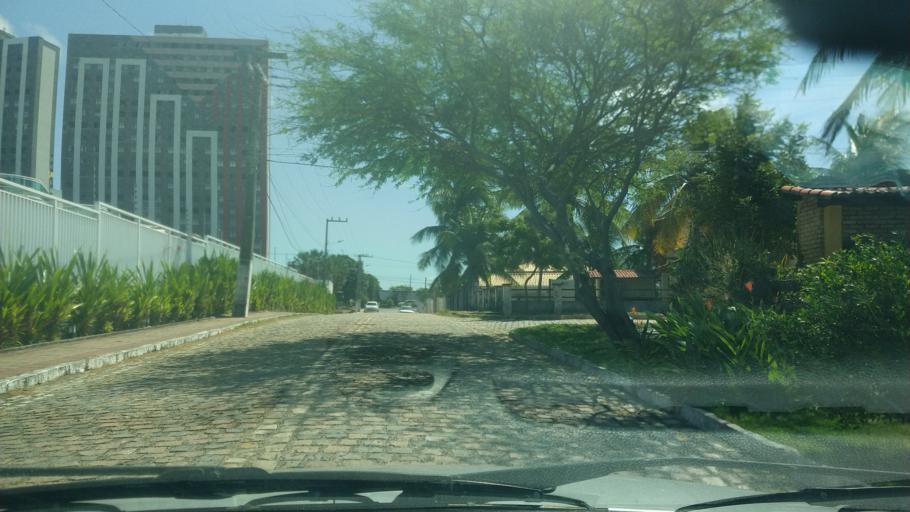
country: BR
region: Rio Grande do Norte
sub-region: Parnamirim
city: Parnamirim
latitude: -5.9566
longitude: -35.1513
